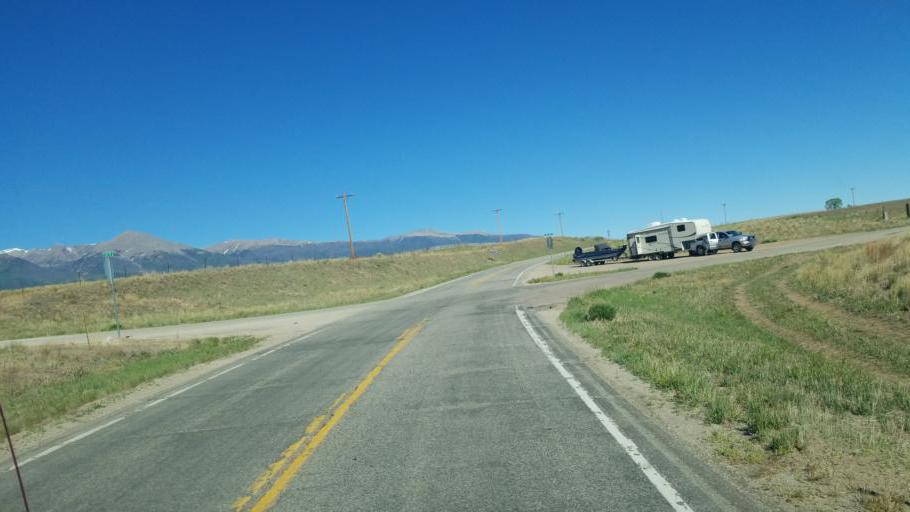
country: US
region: Colorado
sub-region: Custer County
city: Westcliffe
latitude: 38.1700
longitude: -105.5002
